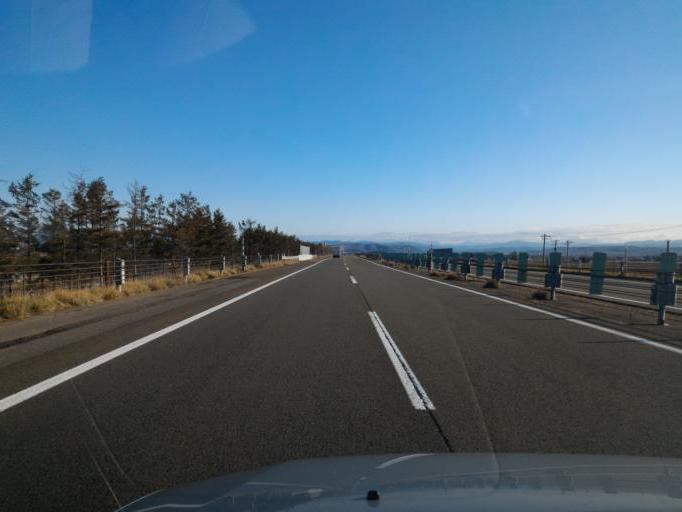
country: JP
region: Hokkaido
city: Iwamizawa
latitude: 43.1515
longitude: 141.7052
